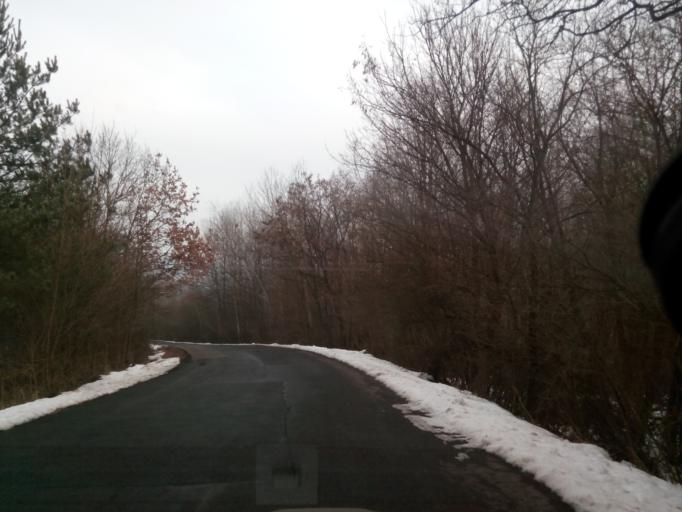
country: HU
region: Borsod-Abauj-Zemplen
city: Gonc
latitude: 48.4845
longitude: 21.3948
